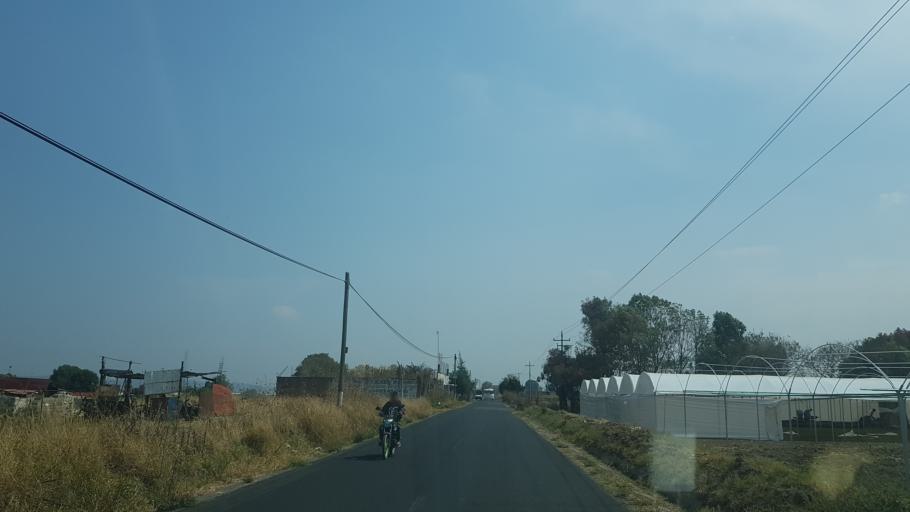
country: MX
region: Puebla
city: San Juan Tianguismanalco
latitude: 18.9410
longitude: -98.4540
